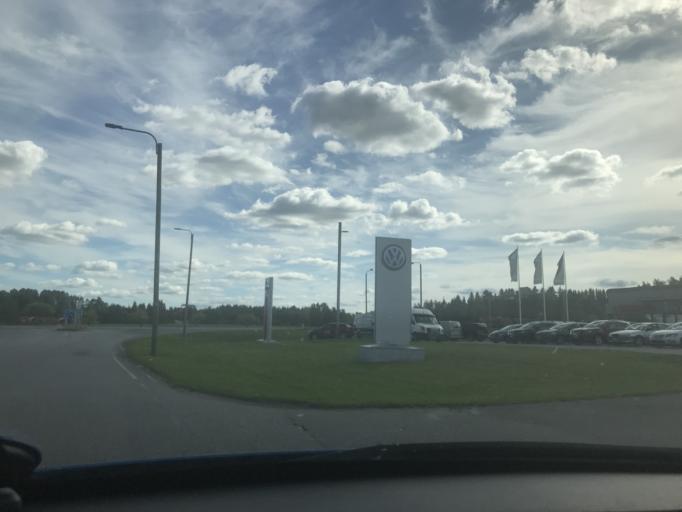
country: FI
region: Southern Ostrobothnia
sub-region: Kuusiokunnat
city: Alavus
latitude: 62.5925
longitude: 23.6033
